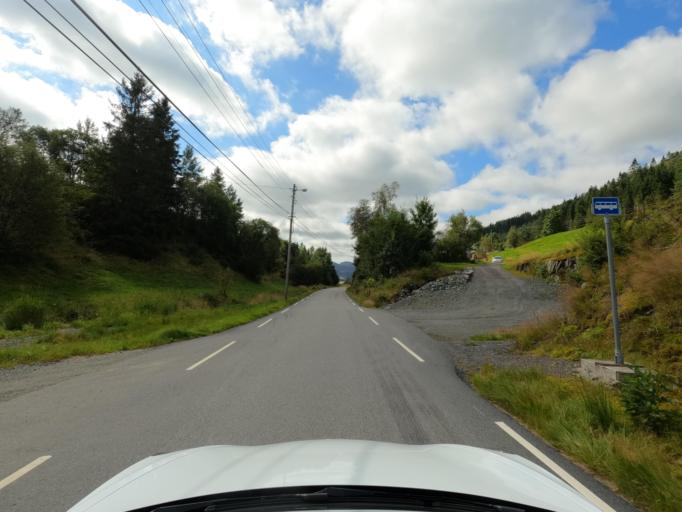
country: NO
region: Hordaland
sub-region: Os
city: Syfteland
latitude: 60.2882
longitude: 5.4739
